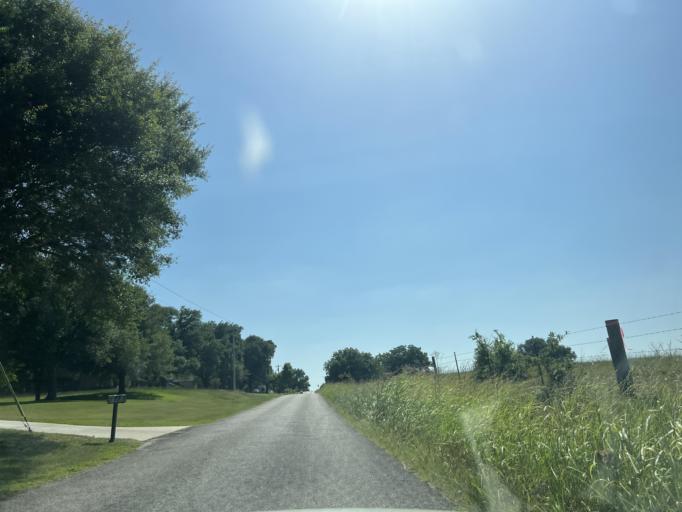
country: US
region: Texas
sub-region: Washington County
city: Brenham
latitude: 30.1542
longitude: -96.3607
